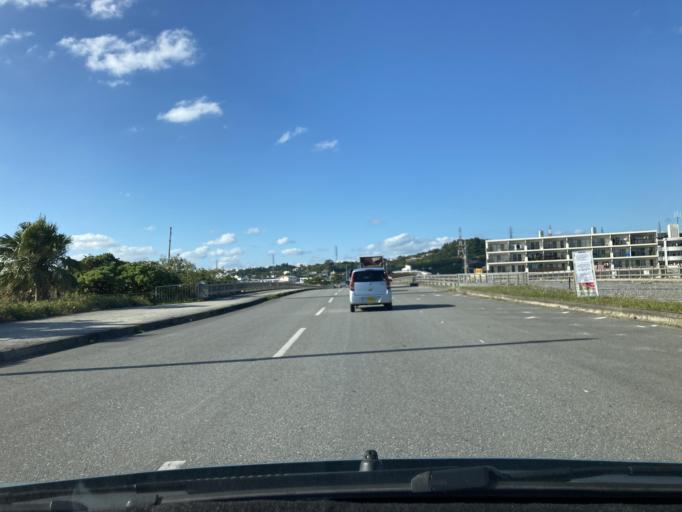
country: JP
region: Okinawa
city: Katsuren-haebaru
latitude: 26.3419
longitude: 127.8574
